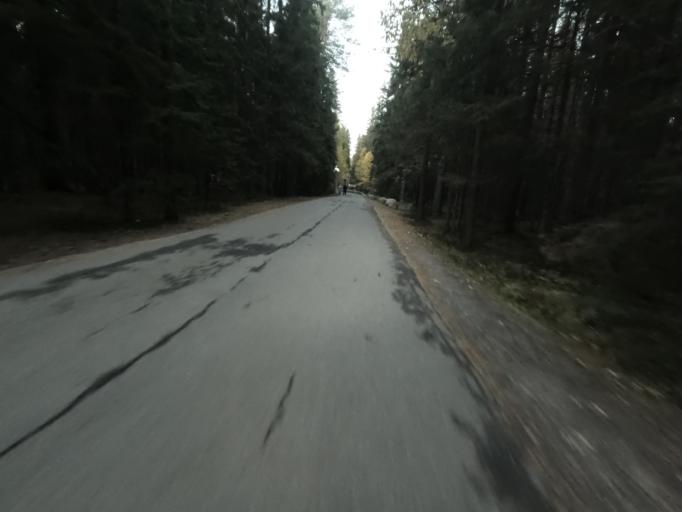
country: RU
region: St.-Petersburg
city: Komarovo
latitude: 60.2055
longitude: 29.8012
